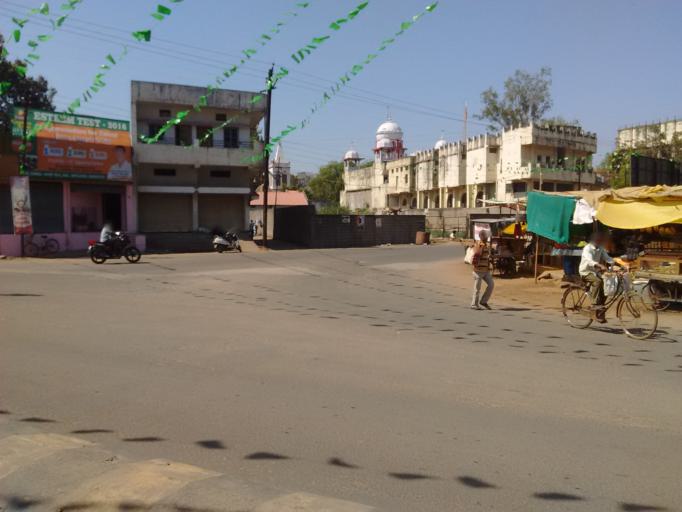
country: IN
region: Maharashtra
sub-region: Gondiya
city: Gondia
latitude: 21.4630
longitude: 80.1962
